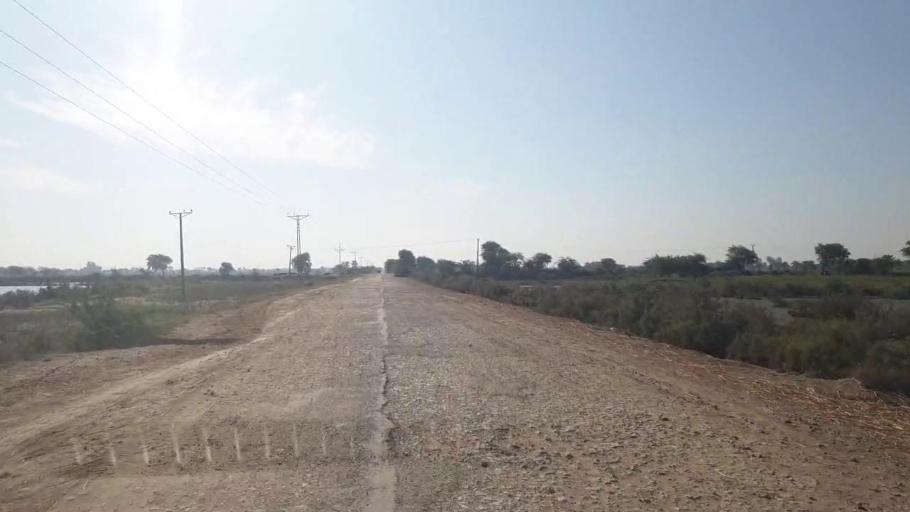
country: PK
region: Sindh
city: Talhar
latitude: 24.9113
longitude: 68.8188
